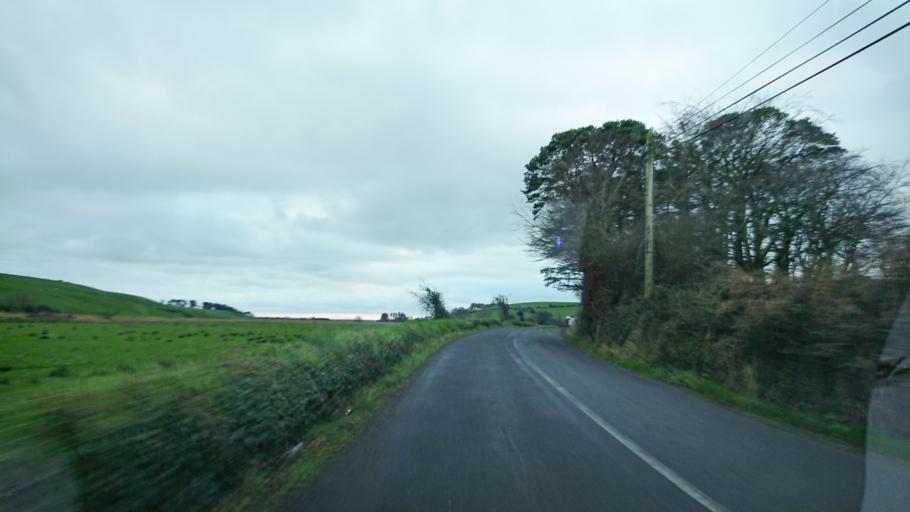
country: IE
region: Munster
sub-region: Waterford
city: Portlaw
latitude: 52.1514
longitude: -7.3798
